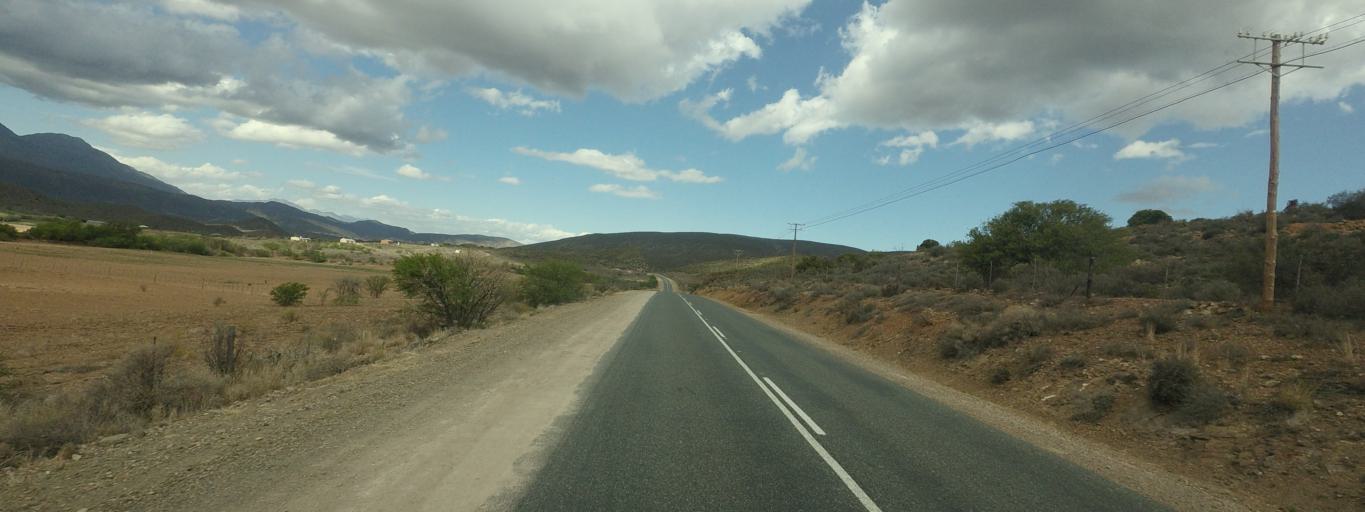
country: ZA
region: Western Cape
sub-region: Eden District Municipality
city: Ladismith
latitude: -33.5013
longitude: 21.4147
